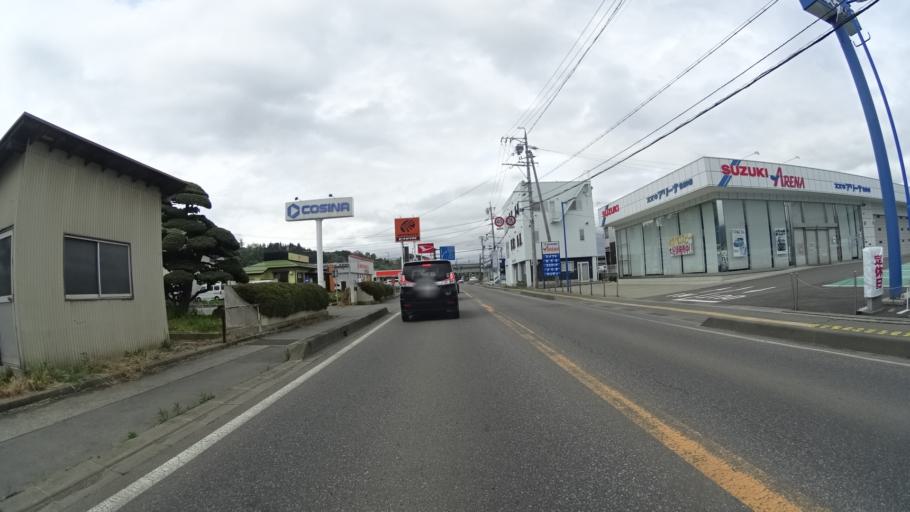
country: JP
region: Nagano
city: Nakano
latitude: 36.7509
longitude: 138.3504
